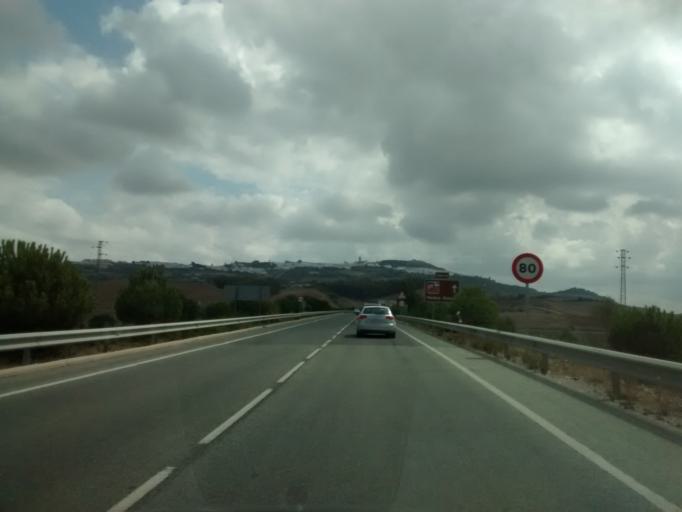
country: ES
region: Andalusia
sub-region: Provincia de Cadiz
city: Medina Sidonia
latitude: 36.4558
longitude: -5.9562
